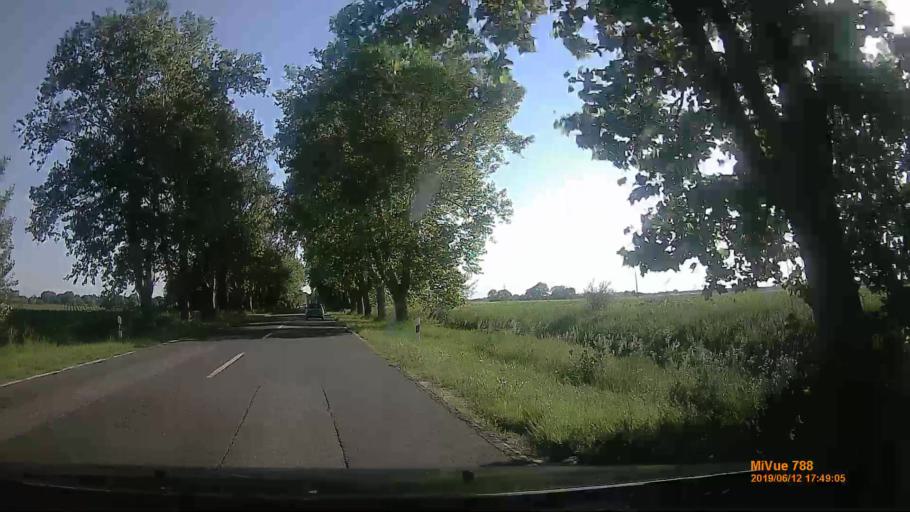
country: HU
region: Csongrad
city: Roszke
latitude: 46.2159
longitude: 20.0599
